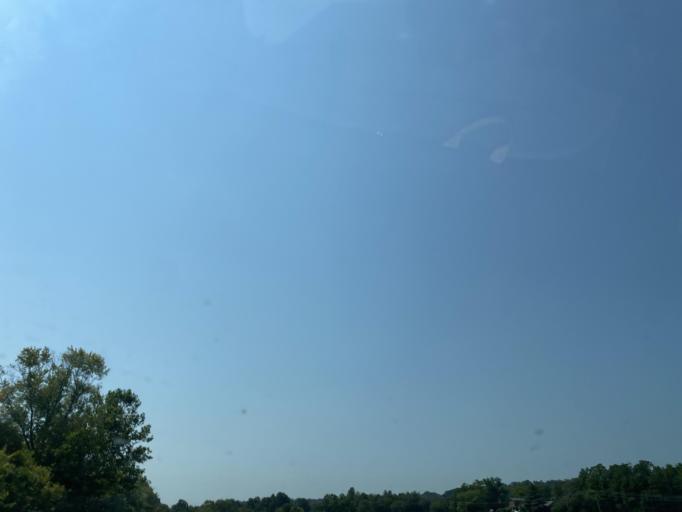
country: US
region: Kentucky
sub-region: Campbell County
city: Claryville
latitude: 38.8375
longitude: -84.4586
